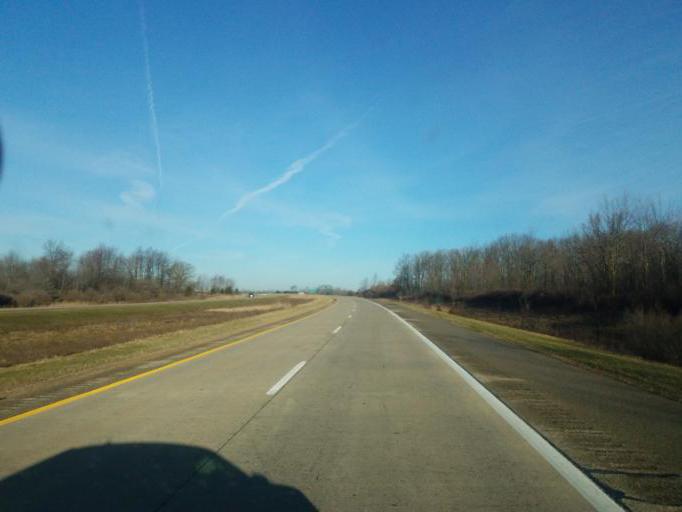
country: US
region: Michigan
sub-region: Clinton County
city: Saint Johns
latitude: 43.0221
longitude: -84.5284
